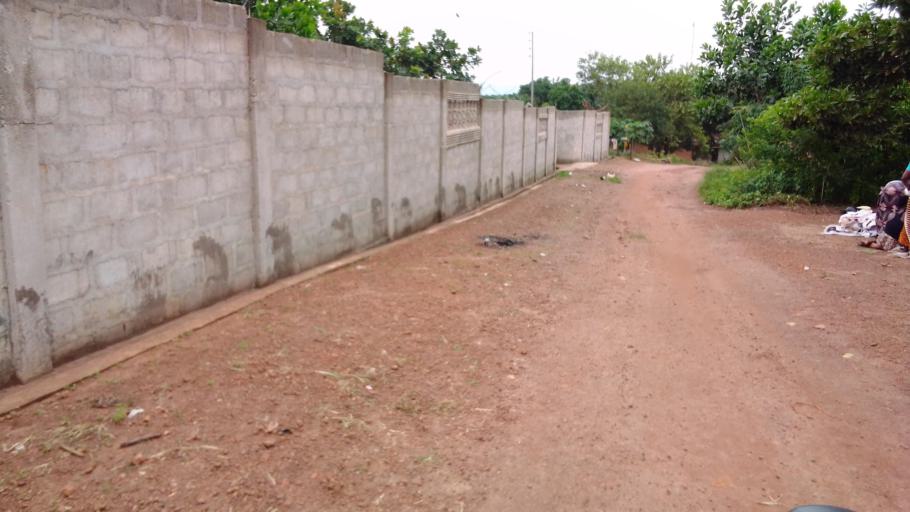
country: SL
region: Eastern Province
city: Kenema
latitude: 7.8570
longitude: -11.1770
